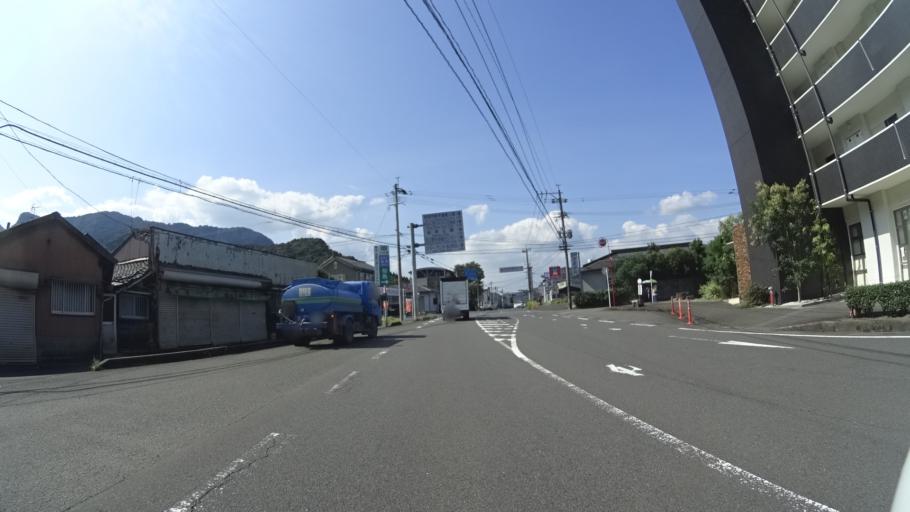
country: JP
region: Kagoshima
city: Kajiki
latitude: 31.7110
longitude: 130.6020
